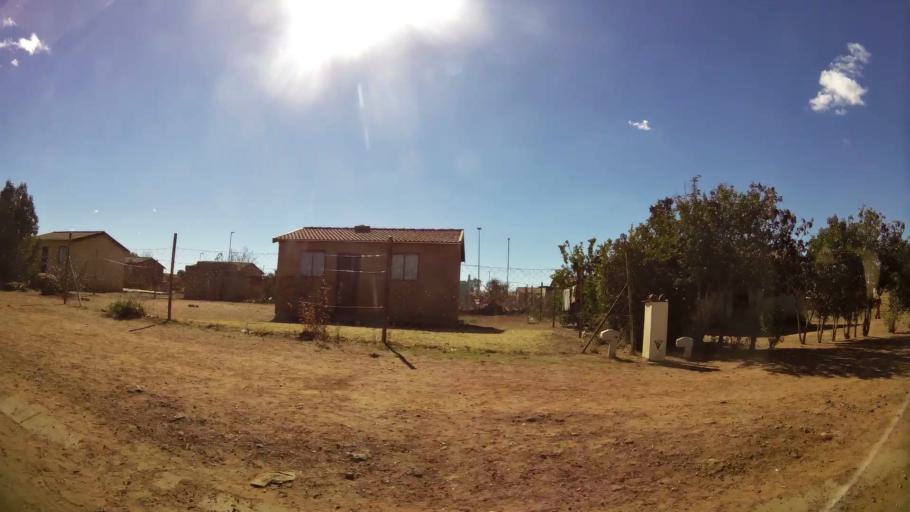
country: ZA
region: North-West
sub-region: Dr Kenneth Kaunda District Municipality
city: Klerksdorp
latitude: -26.8745
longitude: 26.5731
